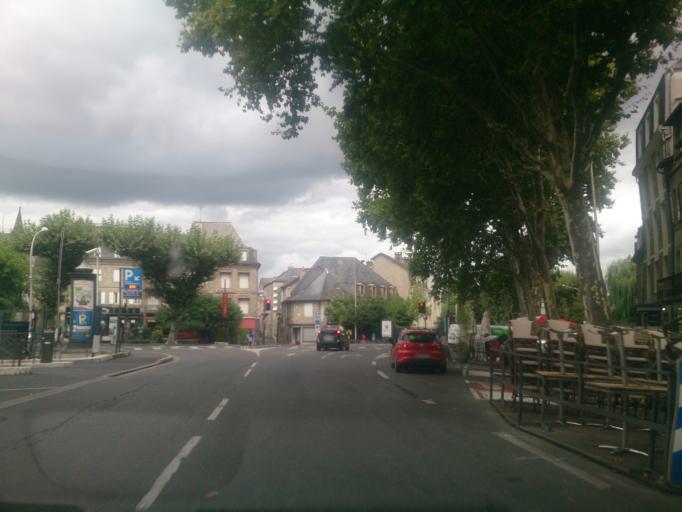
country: FR
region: Limousin
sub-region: Departement de la Correze
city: Brive-la-Gaillarde
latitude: 45.1568
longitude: 1.5361
